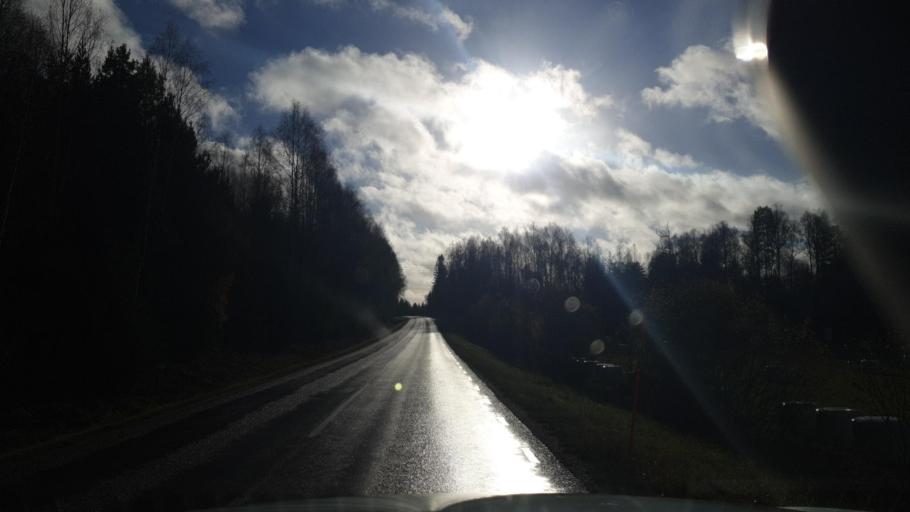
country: SE
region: Vaermland
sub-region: Grums Kommun
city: Slottsbron
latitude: 59.4190
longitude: 12.9829
